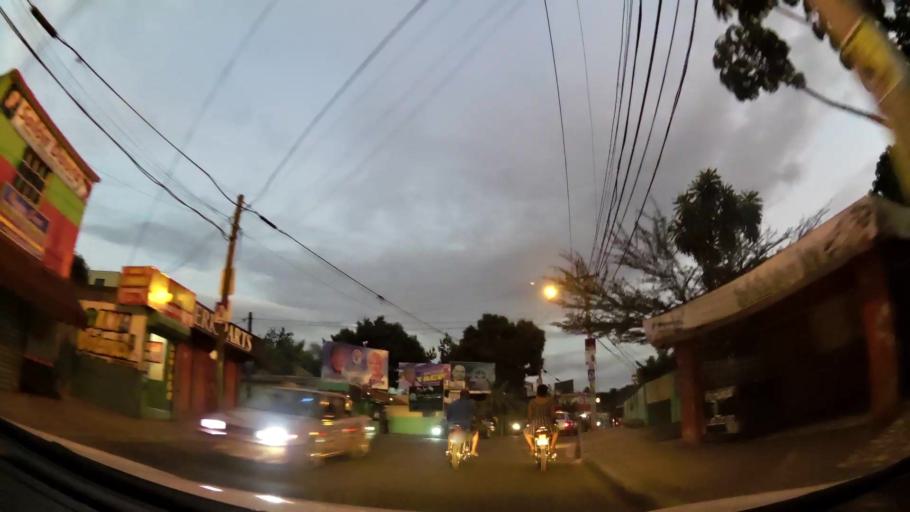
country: DO
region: Santo Domingo
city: Santo Domingo Oeste
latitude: 18.5229
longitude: -70.0190
